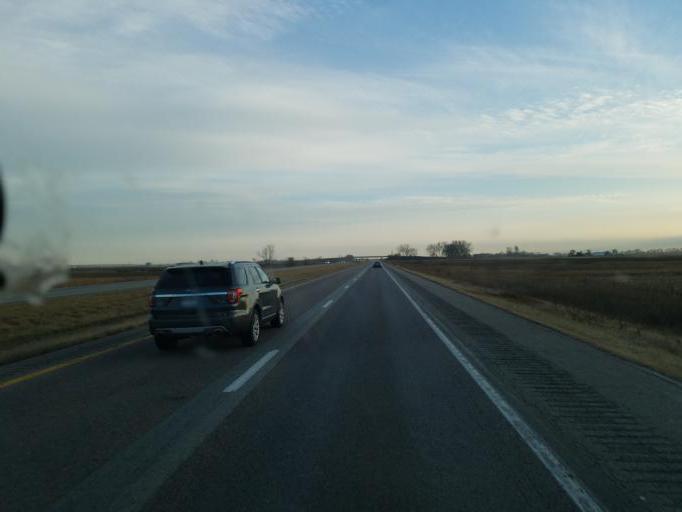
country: US
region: Nebraska
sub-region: Washington County
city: Blair
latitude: 41.6751
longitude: -96.0381
